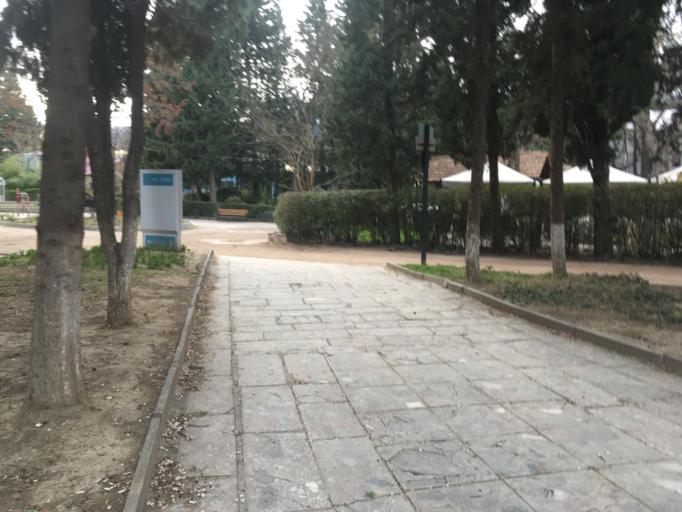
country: GE
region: T'bilisi
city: Tbilisi
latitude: 41.7088
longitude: 44.7998
